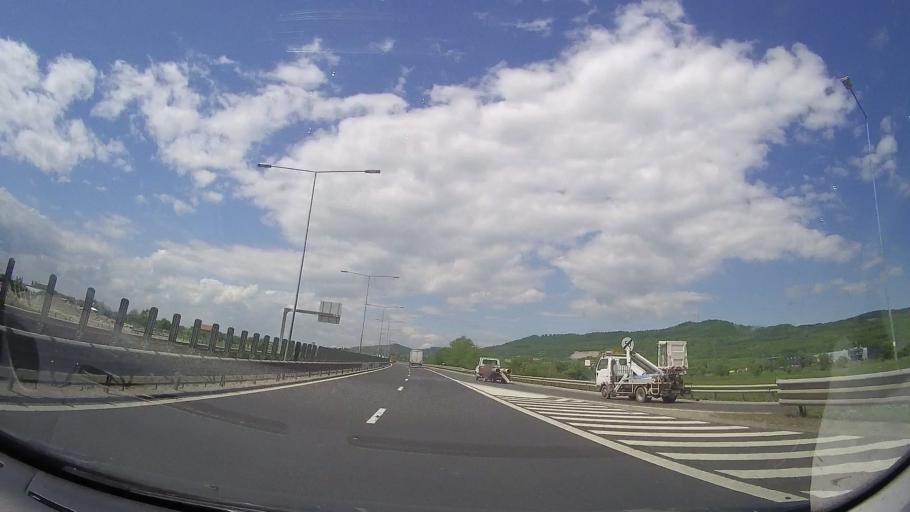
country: RO
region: Sibiu
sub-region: Comuna Selimbar
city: Selimbar
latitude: 45.7912
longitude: 24.1983
